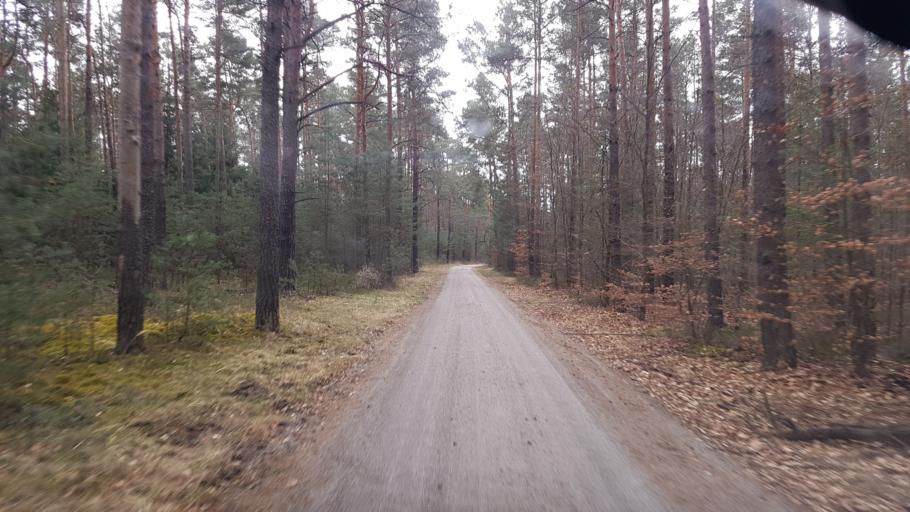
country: DE
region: Brandenburg
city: Finsterwalde
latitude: 51.5720
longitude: 13.7043
